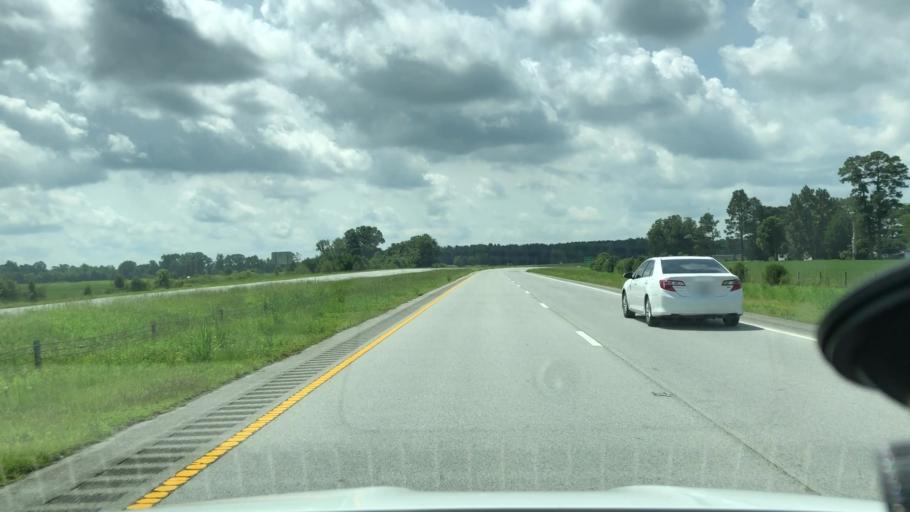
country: US
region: North Carolina
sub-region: Beaufort County
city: Washington
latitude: 35.5131
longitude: -77.0866
